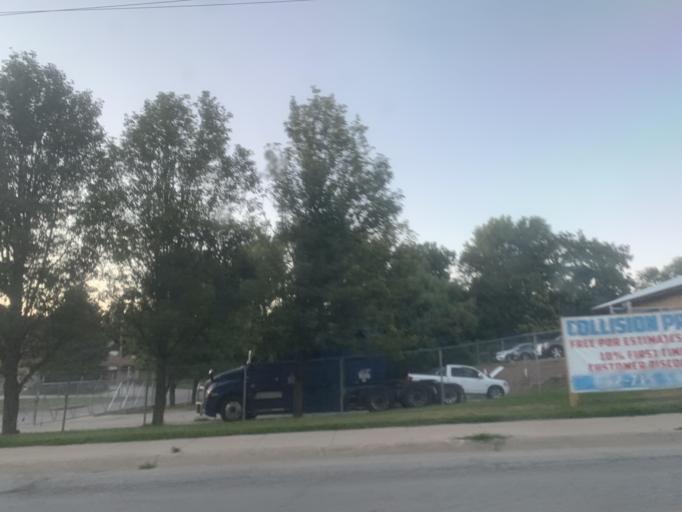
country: US
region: Nebraska
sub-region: Sarpy County
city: La Vista
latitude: 41.2053
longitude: -95.9909
